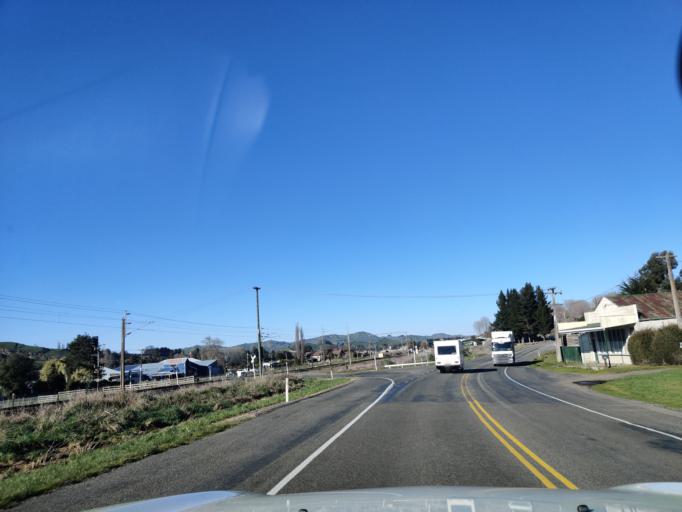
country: NZ
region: Manawatu-Wanganui
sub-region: Ruapehu District
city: Waiouru
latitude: -39.7328
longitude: 175.8440
